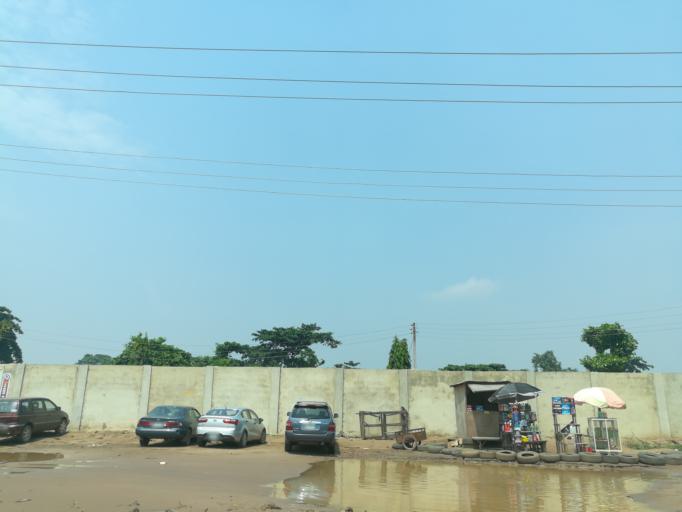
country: NG
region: Lagos
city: Ikorodu
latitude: 6.6338
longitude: 3.4827
